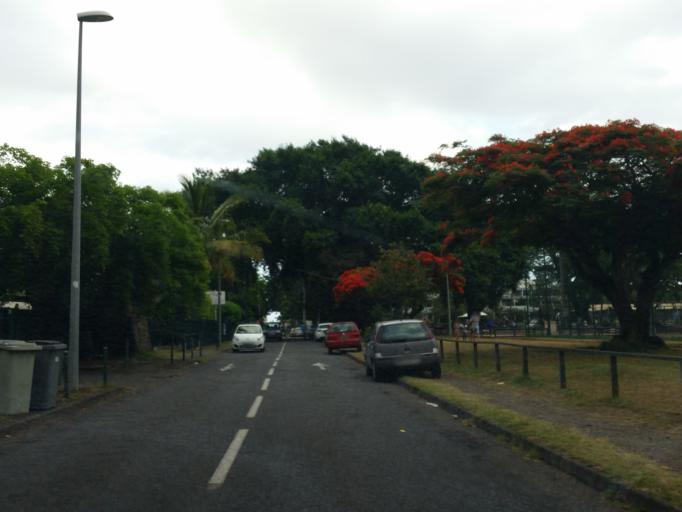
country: RE
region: Reunion
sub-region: Reunion
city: Saint-Denis
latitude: -20.8900
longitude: 55.4659
